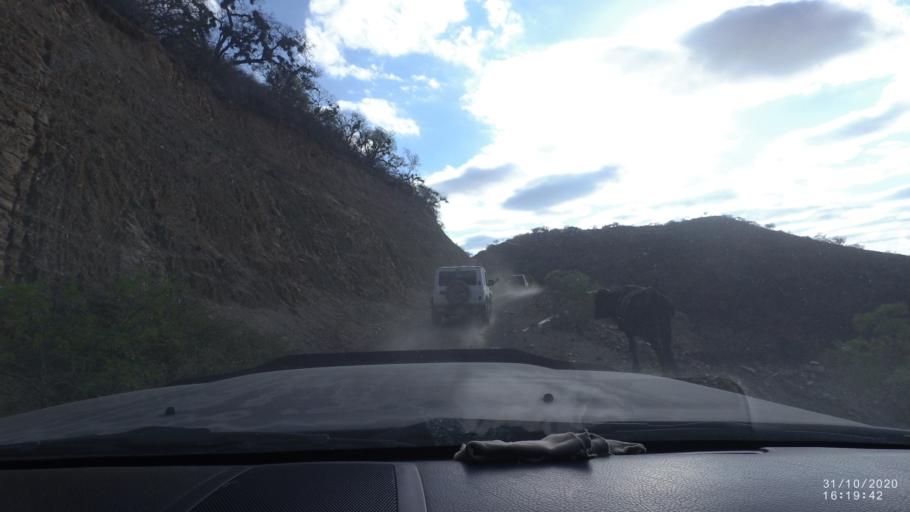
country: BO
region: Chuquisaca
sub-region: Provincia Zudanez
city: Mojocoya
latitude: -18.3968
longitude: -64.6023
